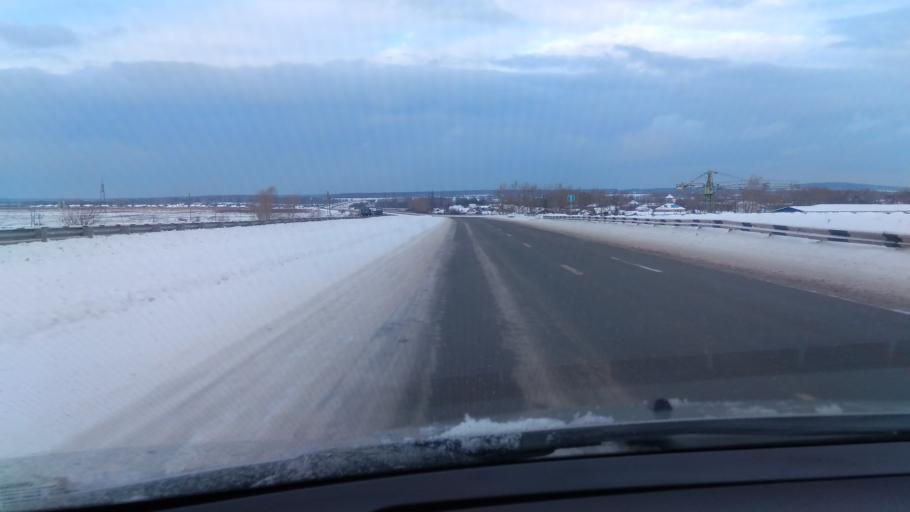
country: RU
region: Sverdlovsk
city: Tsementnyy
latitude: 57.4832
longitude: 60.1802
